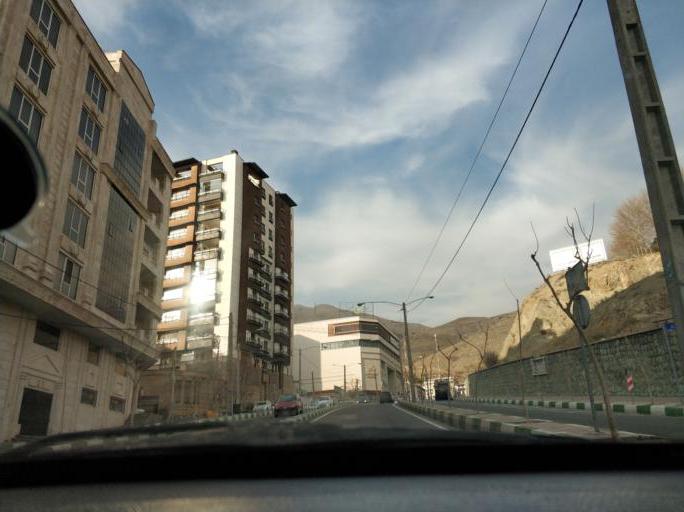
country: IR
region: Tehran
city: Tajrish
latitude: 35.8142
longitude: 51.4846
